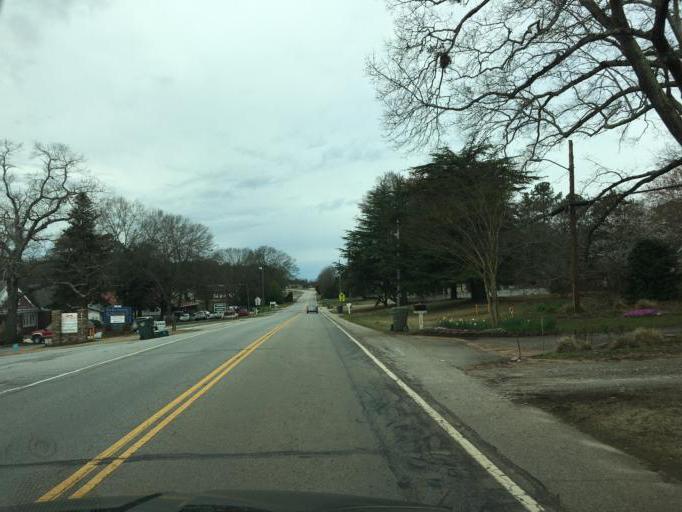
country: US
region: South Carolina
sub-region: Pickens County
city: Clemson
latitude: 34.6732
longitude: -82.8111
